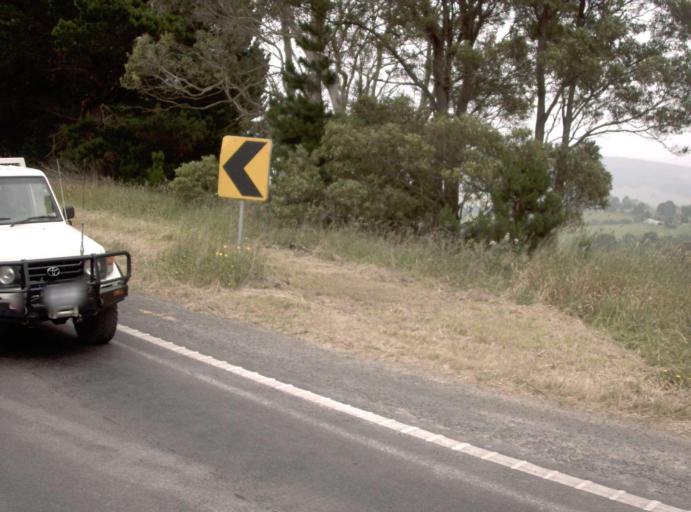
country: AU
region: Victoria
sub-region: Latrobe
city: Moe
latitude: -38.3870
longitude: 146.1250
